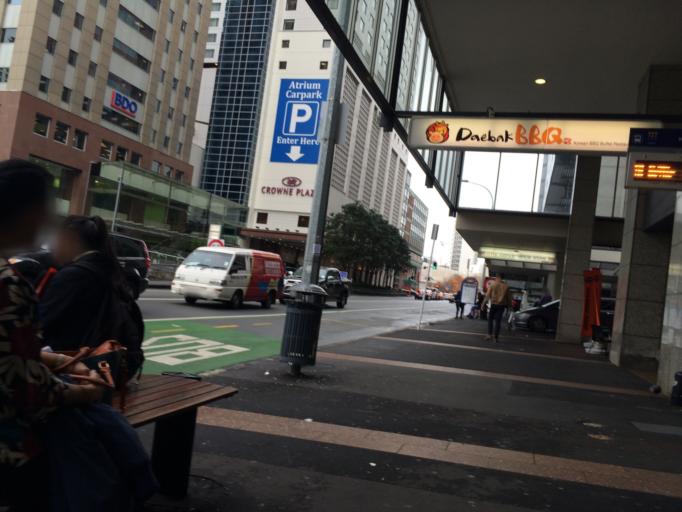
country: NZ
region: Auckland
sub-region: Auckland
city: Auckland
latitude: -36.8489
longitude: 174.7633
